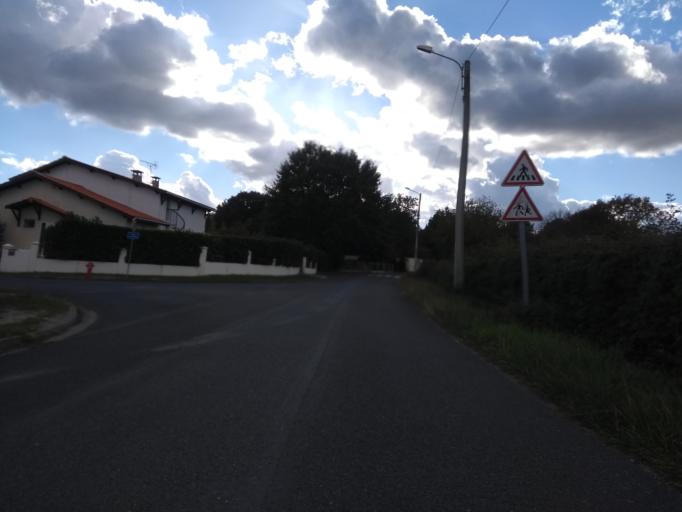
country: FR
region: Aquitaine
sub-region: Departement de la Gironde
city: Cestas
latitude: 44.7394
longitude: -0.6622
